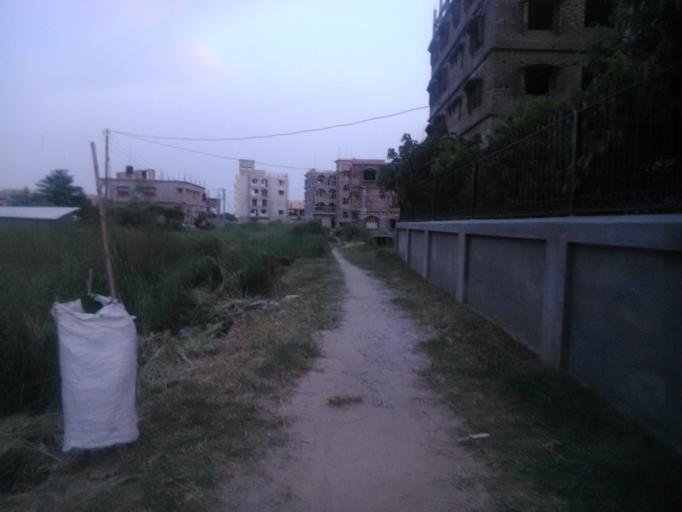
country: IN
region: West Bengal
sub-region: Nadia
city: Navadwip
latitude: 23.4328
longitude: 88.3908
